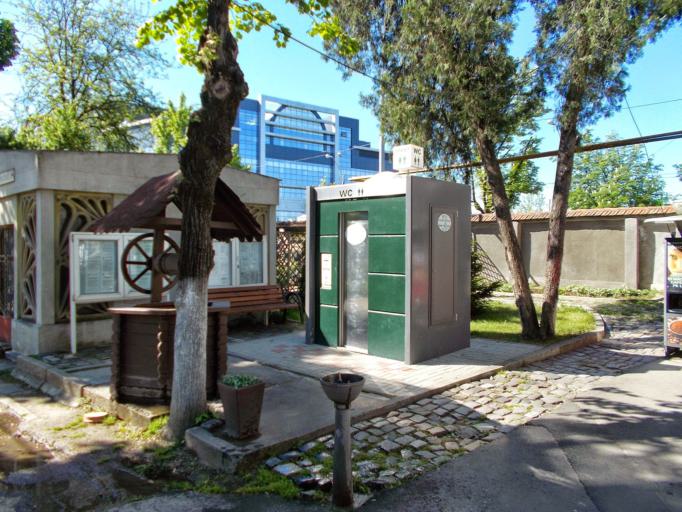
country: RO
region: Bucuresti
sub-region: Municipiul Bucuresti
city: Bucuresti
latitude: 44.4031
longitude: 26.0983
